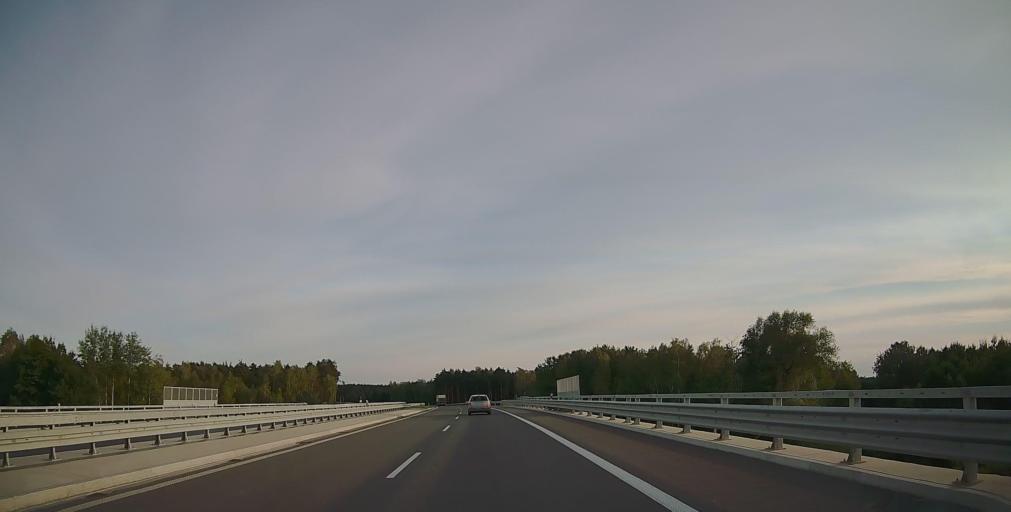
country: PL
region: Masovian Voivodeship
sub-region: Powiat piaseczynski
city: Baniocha
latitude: 51.9866
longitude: 21.1722
